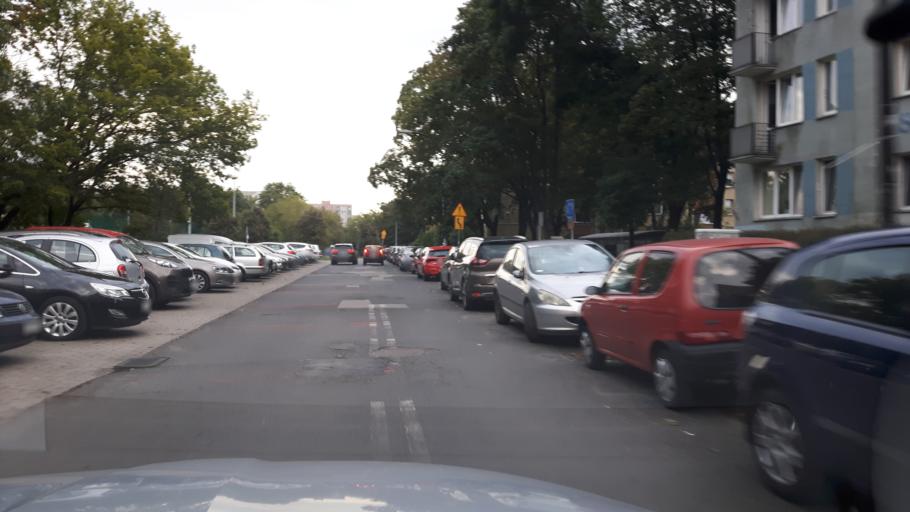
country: PL
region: Masovian Voivodeship
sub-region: Warszawa
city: Targowek
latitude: 52.2948
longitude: 21.0369
